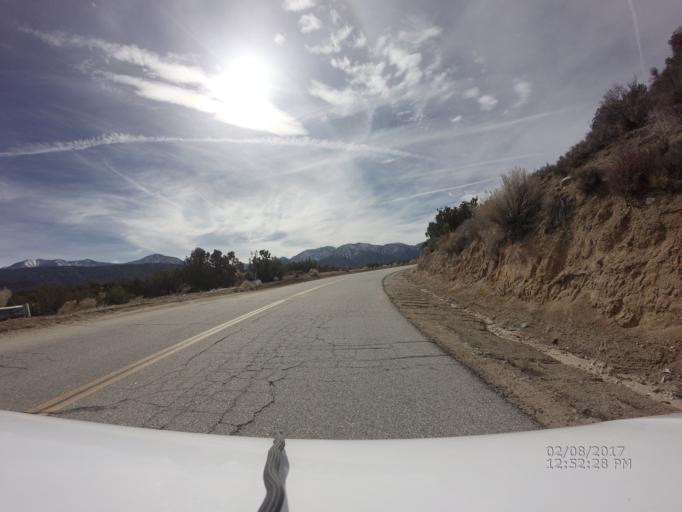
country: US
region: California
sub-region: Los Angeles County
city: Lake Los Angeles
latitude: 34.4516
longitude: -117.8129
